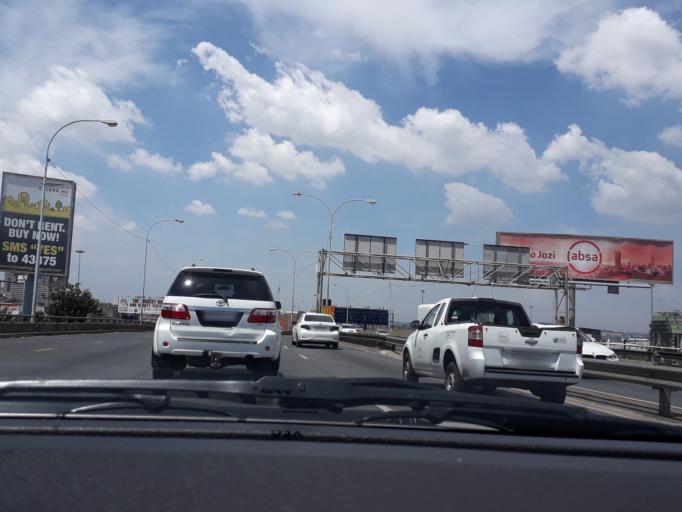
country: ZA
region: Gauteng
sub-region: City of Johannesburg Metropolitan Municipality
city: Johannesburg
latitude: -26.1955
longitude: 28.0285
